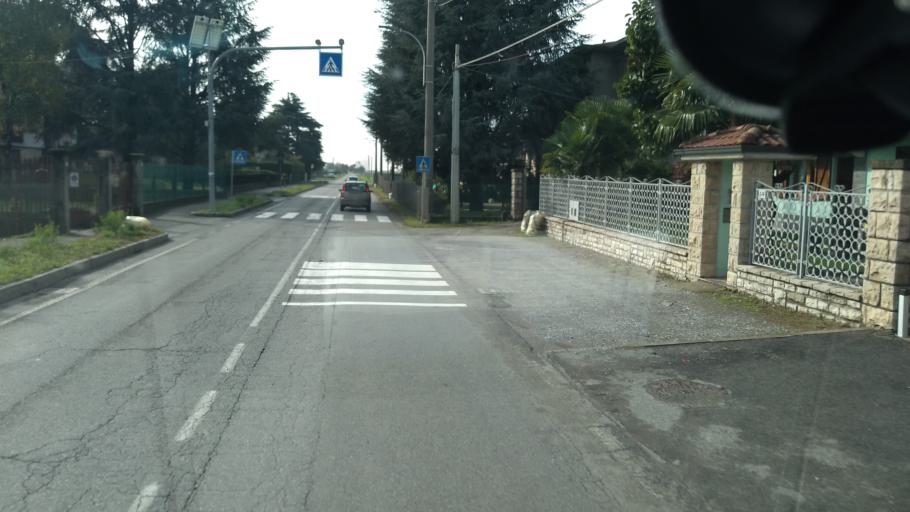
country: IT
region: Lombardy
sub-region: Provincia di Bergamo
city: Cologno al Serio
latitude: 45.5760
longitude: 9.7009
